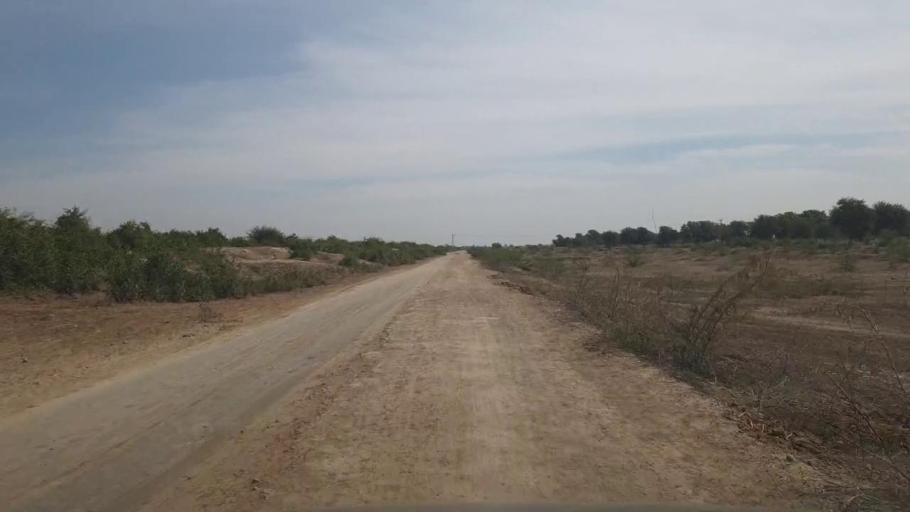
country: PK
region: Sindh
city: Kunri
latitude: 25.2965
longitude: 69.5797
